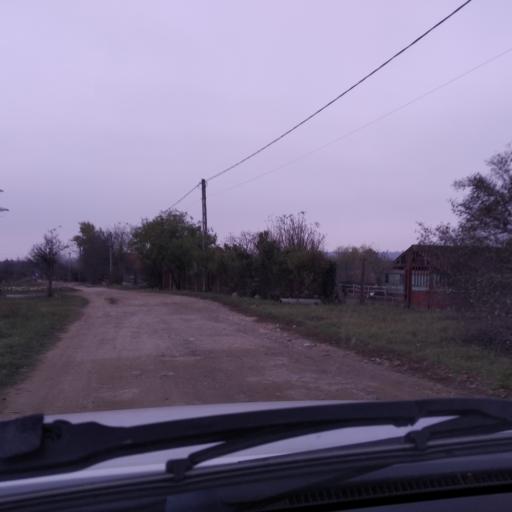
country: HU
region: Pest
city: Pomaz
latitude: 47.6306
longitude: 19.0281
